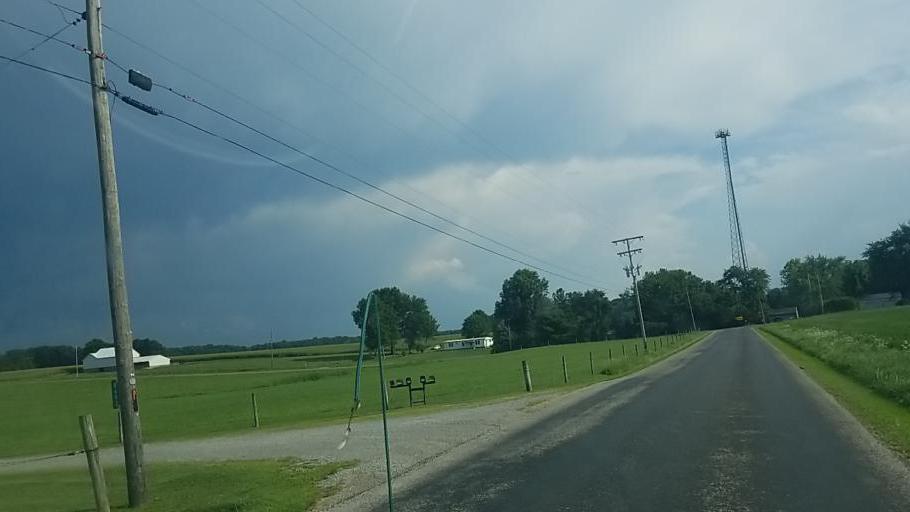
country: US
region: Ohio
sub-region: Wayne County
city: Smithville
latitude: 40.9032
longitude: -81.8592
